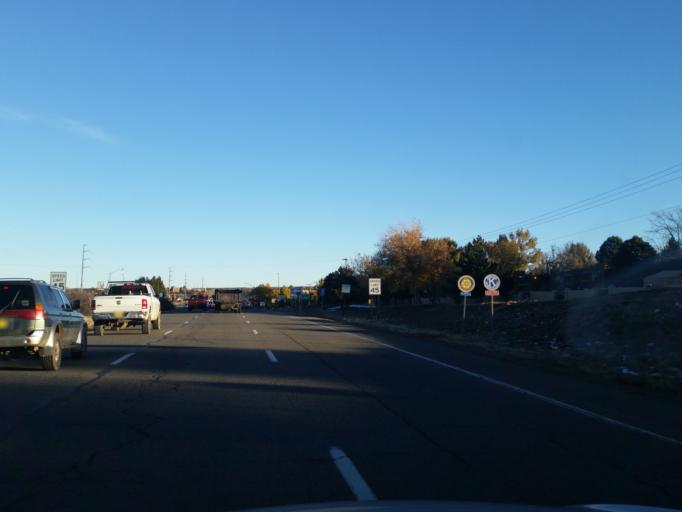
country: US
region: New Mexico
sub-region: Santa Fe County
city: Santa Fe
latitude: 35.6397
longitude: -105.9562
